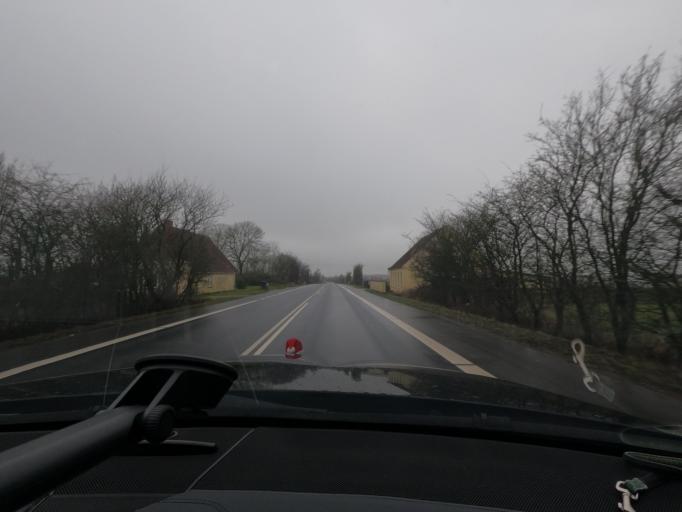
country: DK
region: South Denmark
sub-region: Sonderborg Kommune
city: Horuphav
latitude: 54.9027
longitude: 9.9487
